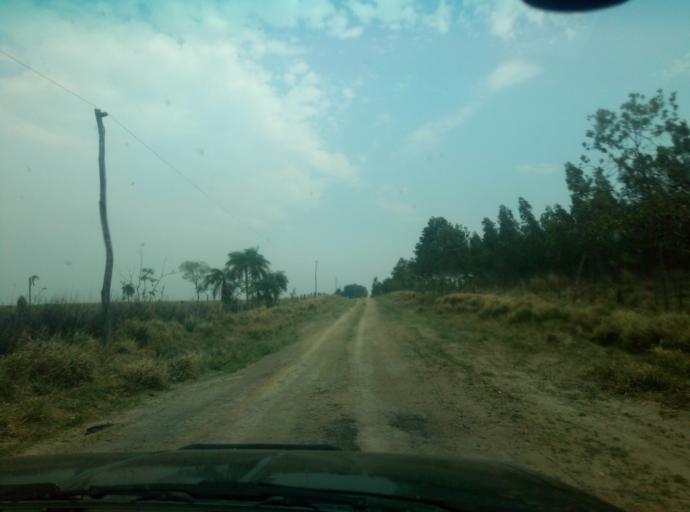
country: PY
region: Caaguazu
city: San Joaquin
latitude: -25.1095
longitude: -56.1275
